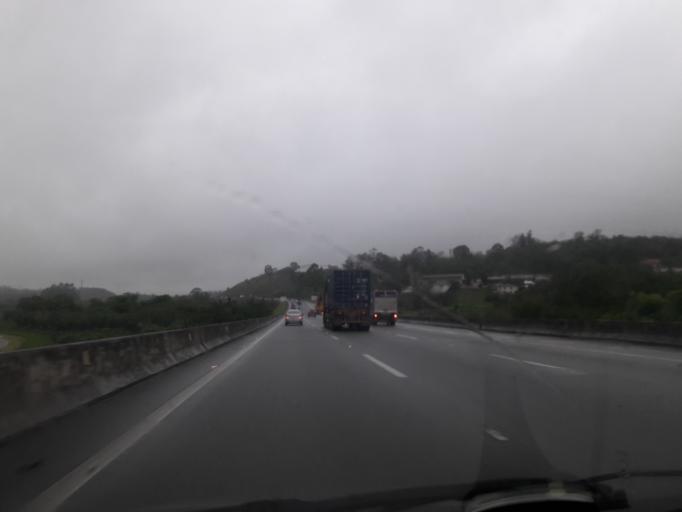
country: BR
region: Sao Paulo
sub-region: Embu
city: Embu
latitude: -23.6505
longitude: -46.8306
